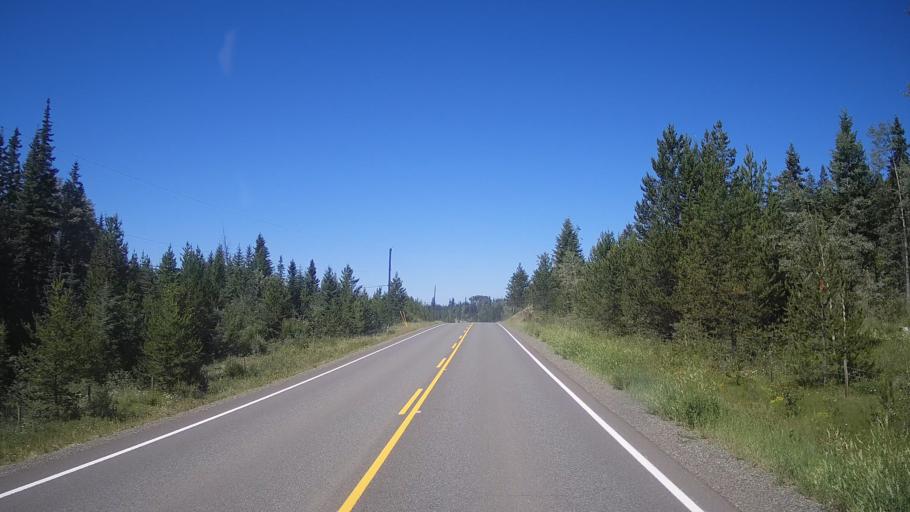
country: CA
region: British Columbia
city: Cache Creek
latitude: 51.5432
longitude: -120.9586
